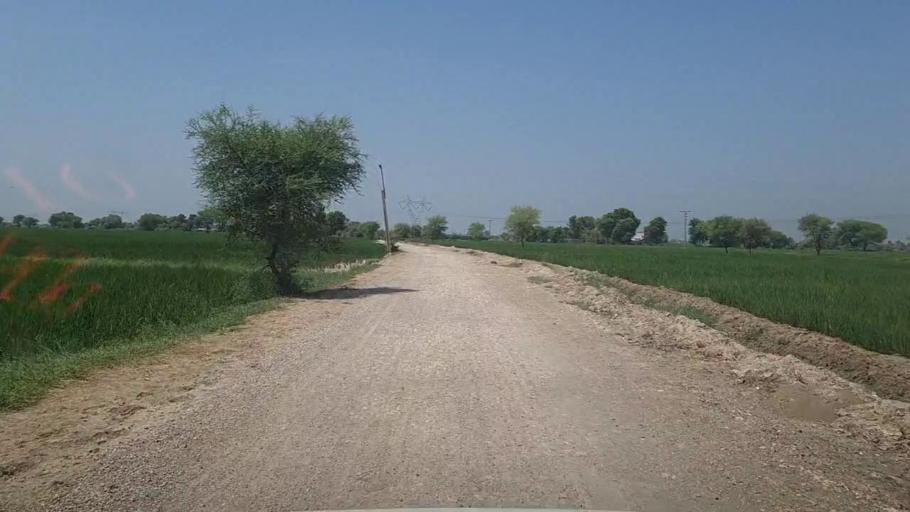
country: PK
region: Sindh
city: Kandhkot
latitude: 28.3194
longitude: 69.3795
